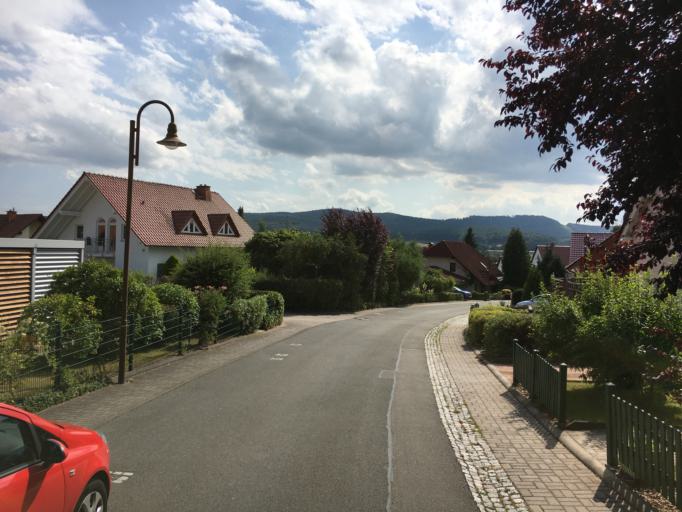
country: DE
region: Thuringia
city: Breitungen
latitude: 50.7630
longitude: 10.3342
